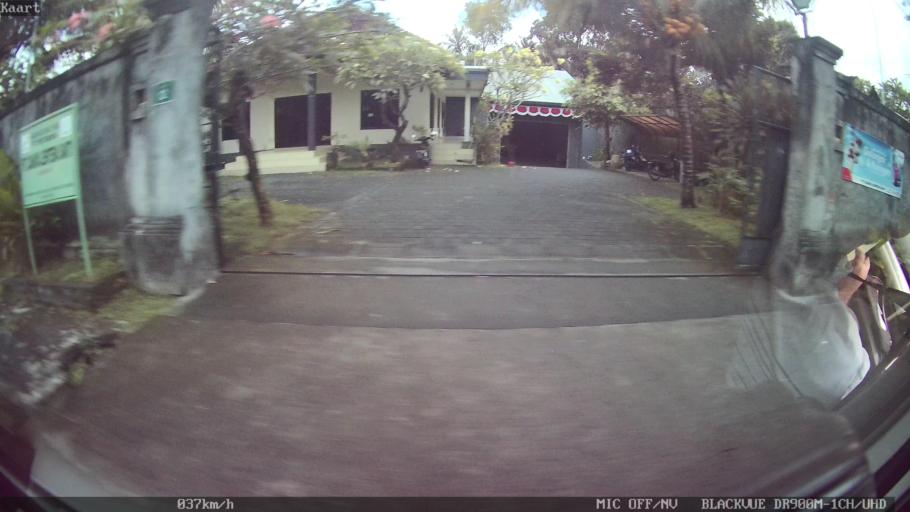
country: ID
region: Bali
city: Banjar Mambalkajanan
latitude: -8.5592
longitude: 115.2079
